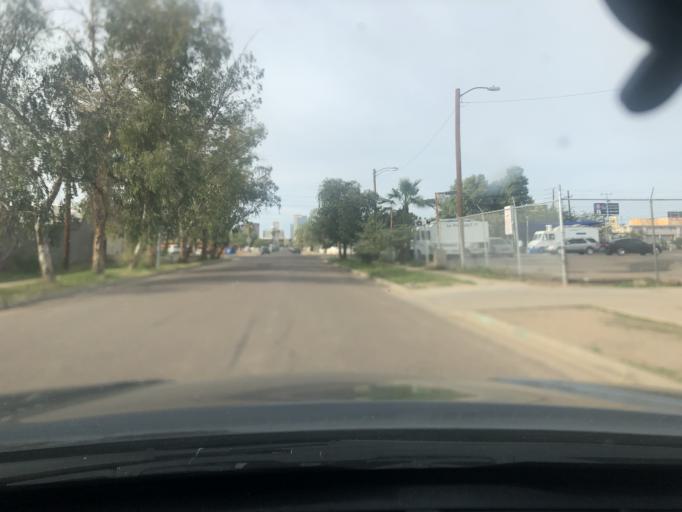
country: US
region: Arizona
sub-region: Maricopa County
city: Phoenix
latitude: 33.4504
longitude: -112.0467
